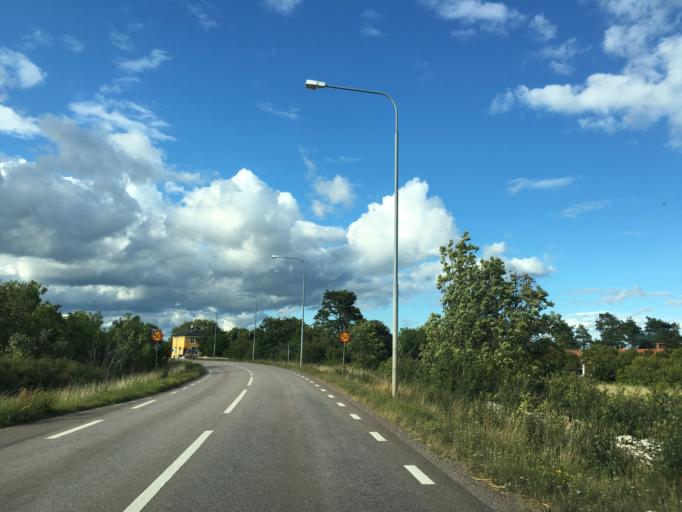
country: SE
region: Kalmar
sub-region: Morbylanga Kommun
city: Moerbylanga
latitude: 56.5368
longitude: 16.4460
